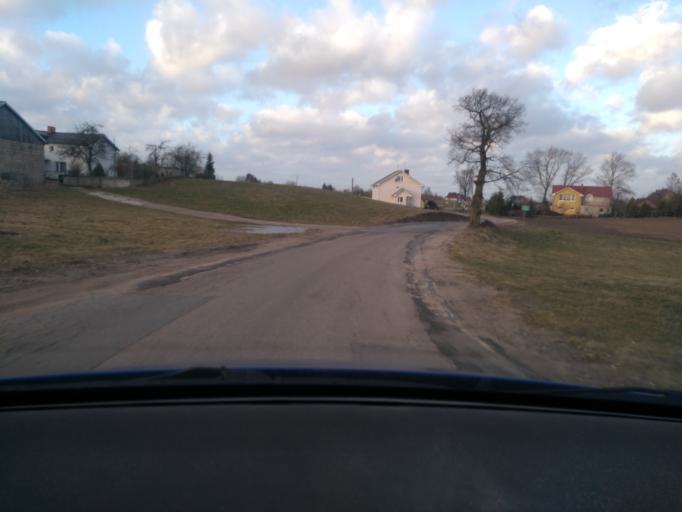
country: PL
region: Pomeranian Voivodeship
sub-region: Powiat kartuski
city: Przodkowo
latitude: 54.3990
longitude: 18.2224
